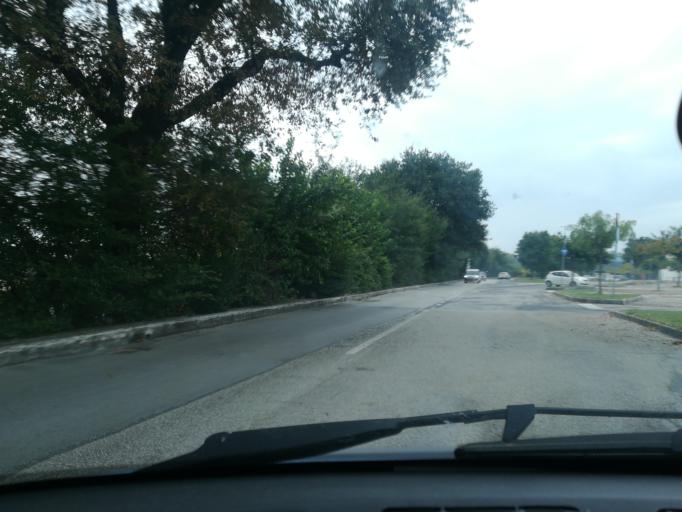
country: IT
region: The Marches
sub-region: Provincia di Macerata
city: Piediripa
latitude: 43.2798
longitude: 13.5044
